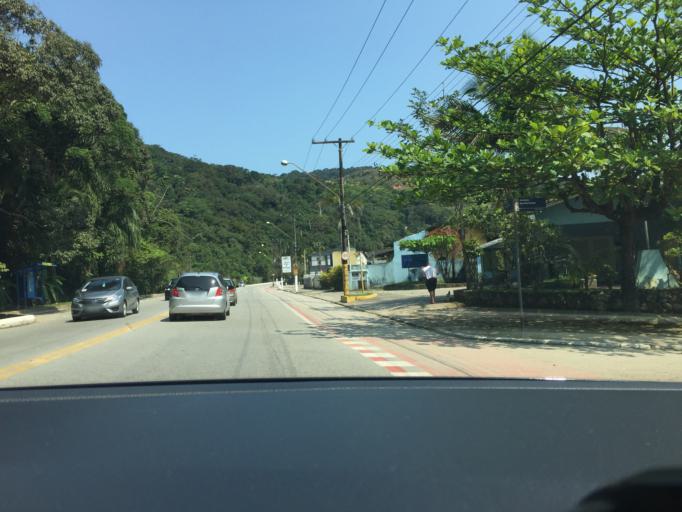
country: BR
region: Sao Paulo
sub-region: Guaruja
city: Guaruja
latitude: -23.9761
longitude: -46.1891
